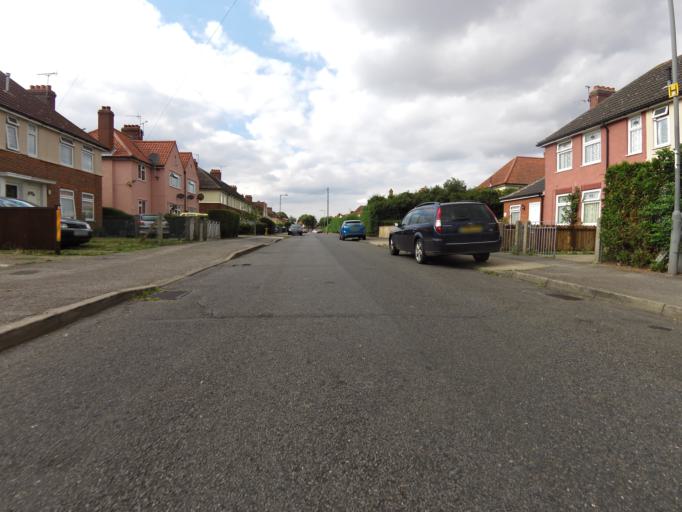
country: GB
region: England
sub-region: Suffolk
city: Bramford
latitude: 52.0831
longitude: 1.1285
